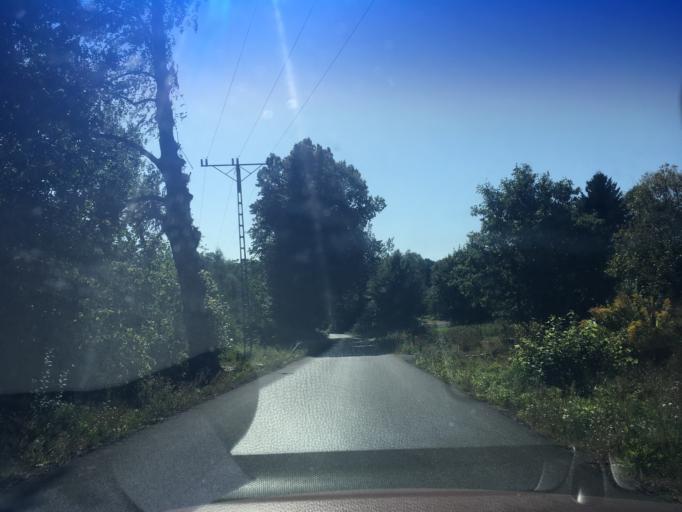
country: PL
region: Lower Silesian Voivodeship
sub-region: Powiat lubanski
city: Lesna
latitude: 51.0151
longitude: 15.1986
